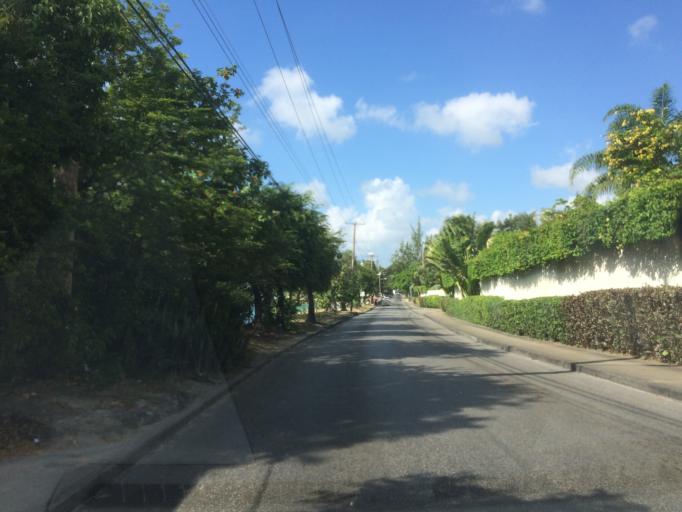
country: BB
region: Saint James
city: Holetown
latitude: 13.1580
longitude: -59.6369
